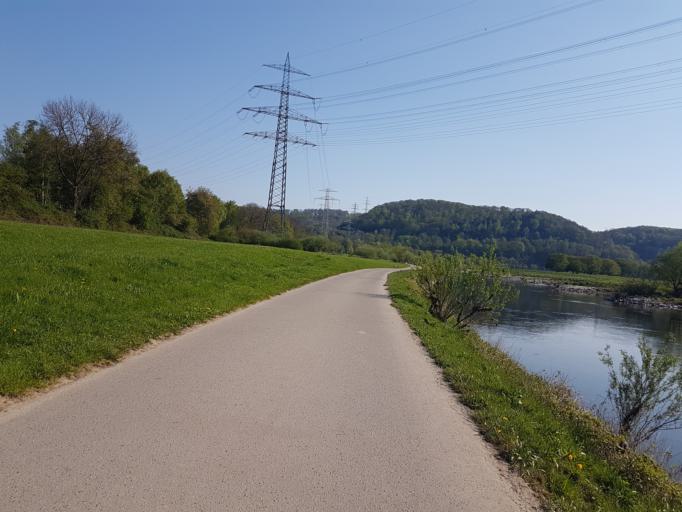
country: DE
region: North Rhine-Westphalia
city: Hattingen
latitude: 51.3964
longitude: 7.1632
